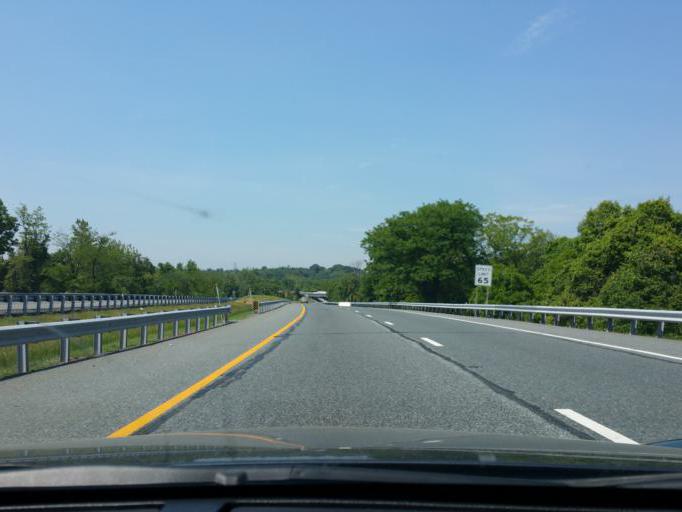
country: US
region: Maryland
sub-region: Howard County
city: Elkridge
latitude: 39.2215
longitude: -76.6944
